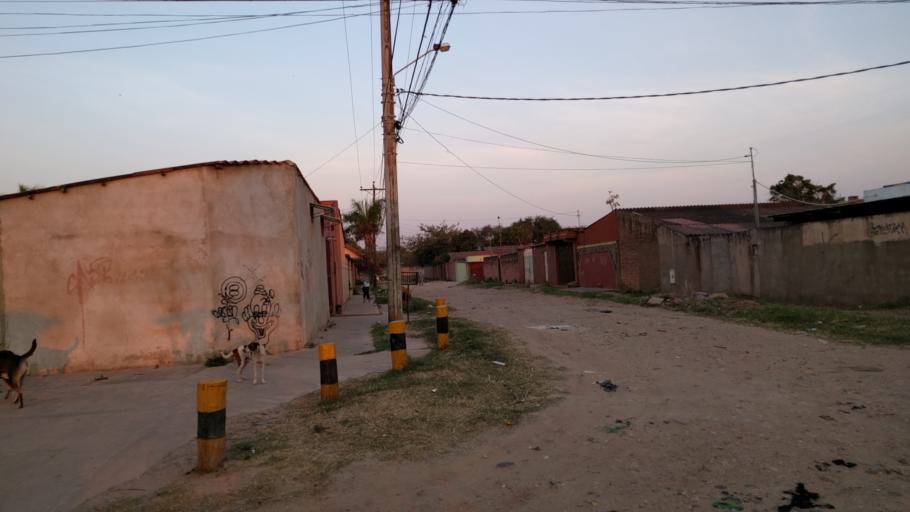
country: BO
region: Santa Cruz
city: Santa Cruz de la Sierra
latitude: -17.7515
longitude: -63.1489
